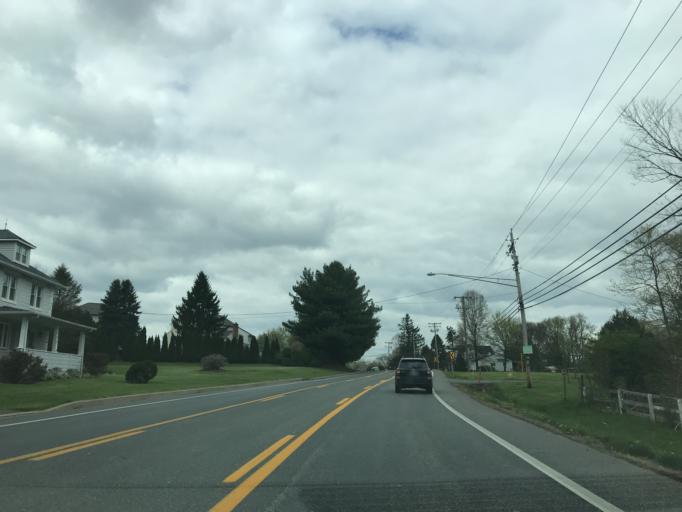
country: US
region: Maryland
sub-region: Harford County
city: Bel Air South
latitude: 39.5324
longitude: -76.2967
